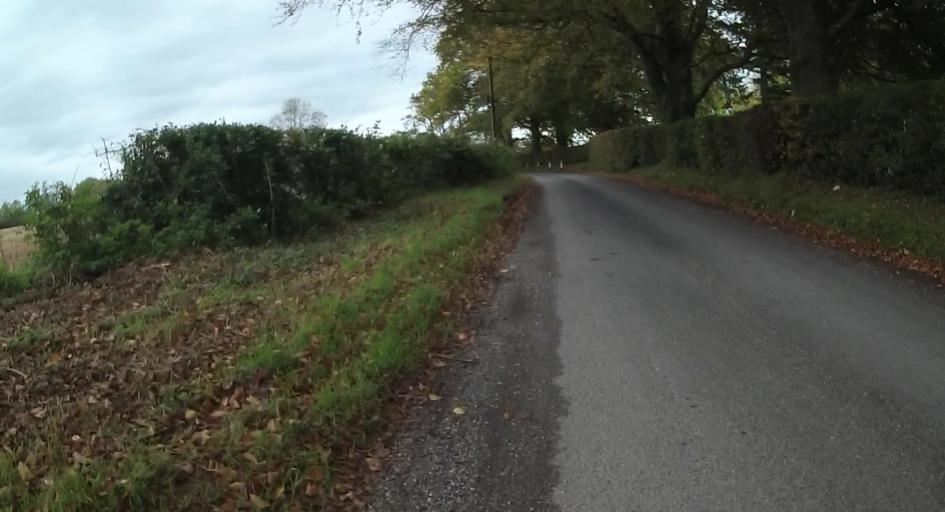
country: GB
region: England
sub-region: Hampshire
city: Four Marks
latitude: 51.1470
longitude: -1.1106
